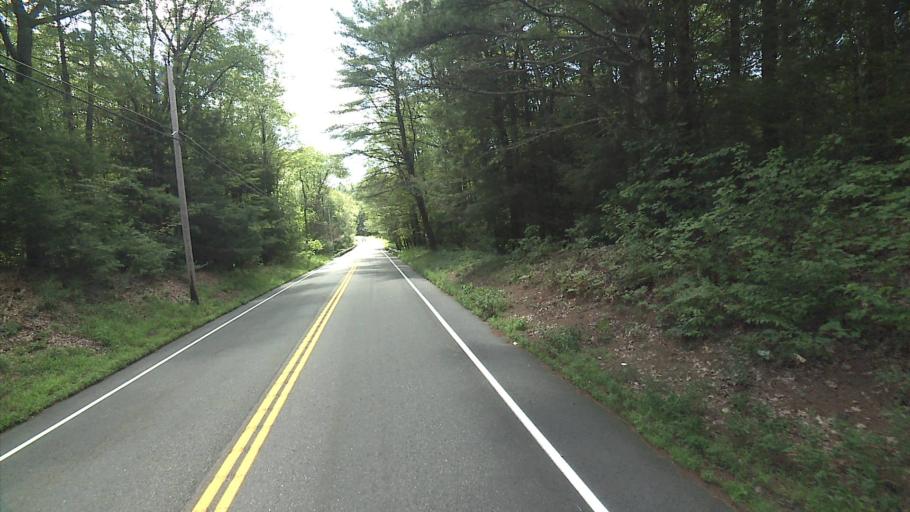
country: US
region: Massachusetts
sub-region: Worcester County
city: Southbridge
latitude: 41.9952
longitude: -72.0835
